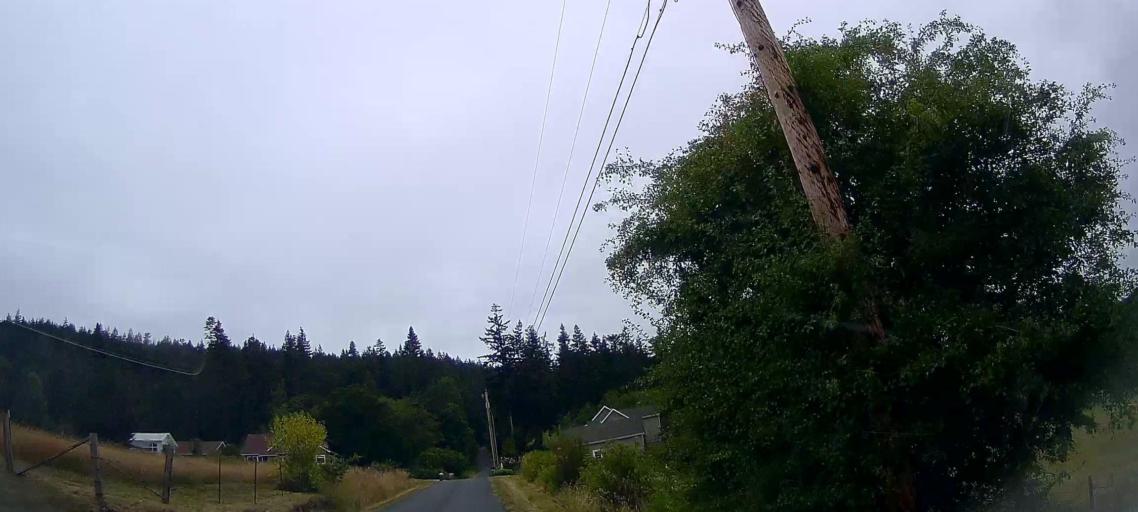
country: US
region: Washington
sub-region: Skagit County
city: Anacortes
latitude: 48.4336
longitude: -122.6204
